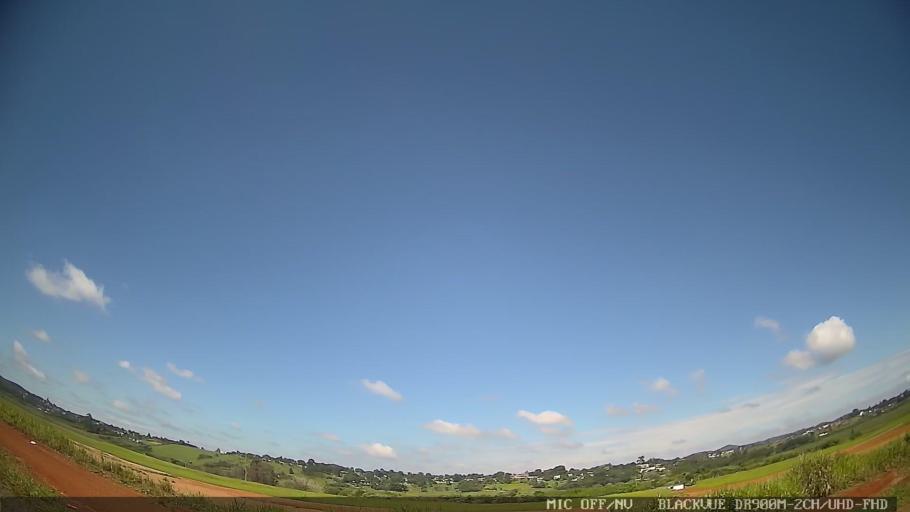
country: BR
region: Sao Paulo
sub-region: Suzano
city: Suzano
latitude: -23.6303
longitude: -46.2564
